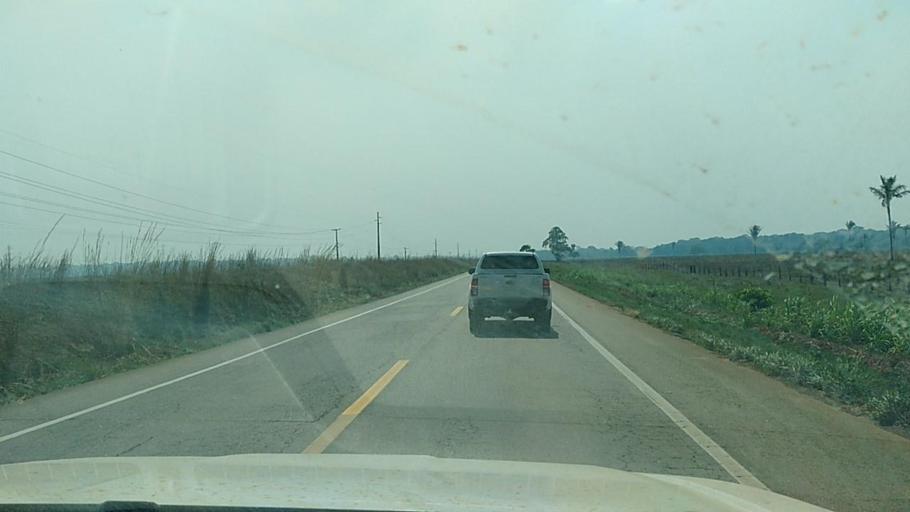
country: BR
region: Rondonia
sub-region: Porto Velho
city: Porto Velho
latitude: -8.7829
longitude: -63.5643
